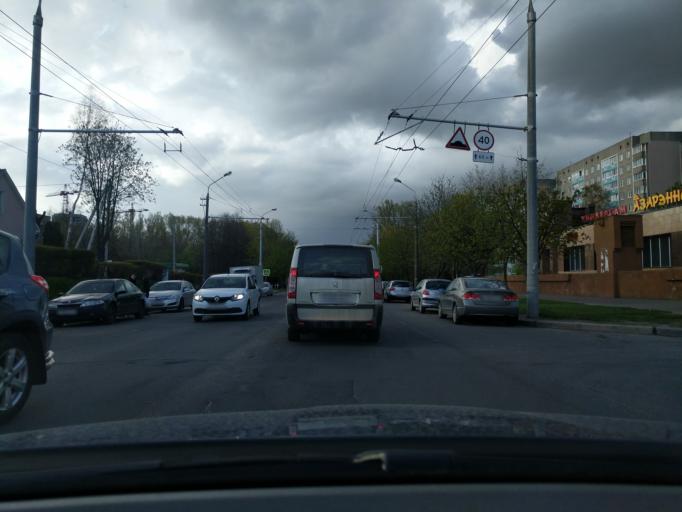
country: BY
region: Minsk
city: Novoye Medvezhino
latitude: 53.8952
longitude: 27.4813
